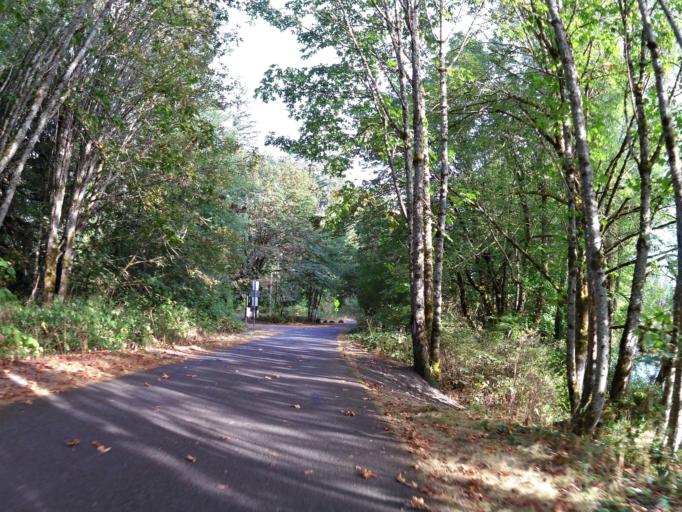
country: US
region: Washington
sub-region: Thurston County
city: Tenino
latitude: 46.9276
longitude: -122.8123
